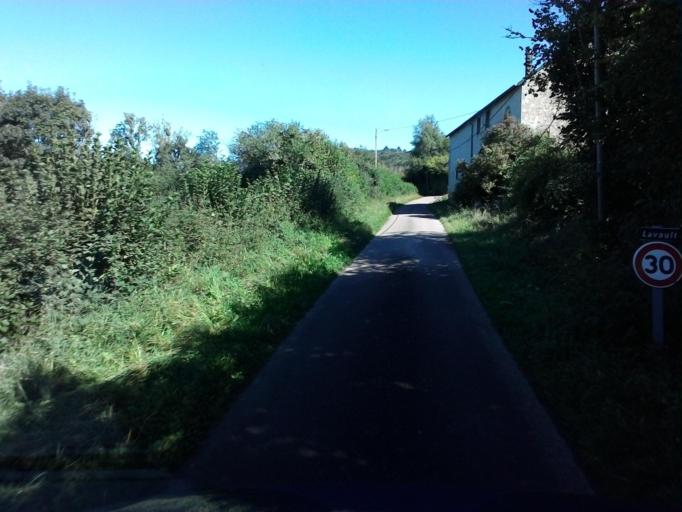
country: FR
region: Bourgogne
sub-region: Departement de la Cote-d'Or
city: Saulieu
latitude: 47.2509
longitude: 4.2099
